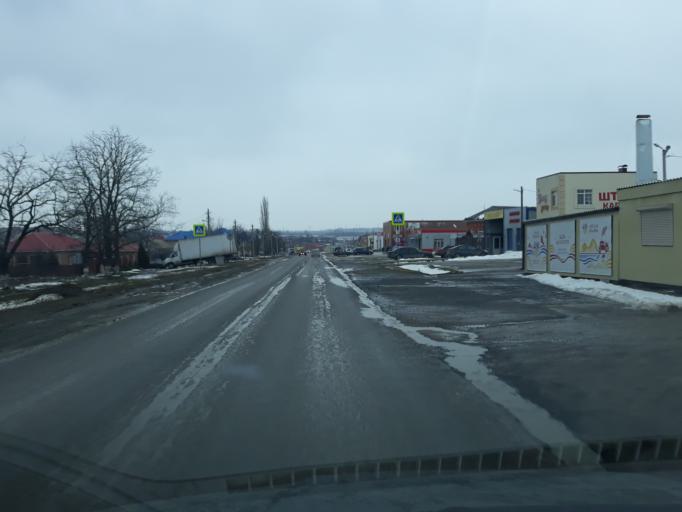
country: RU
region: Rostov
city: Krym
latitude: 47.2814
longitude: 39.5167
